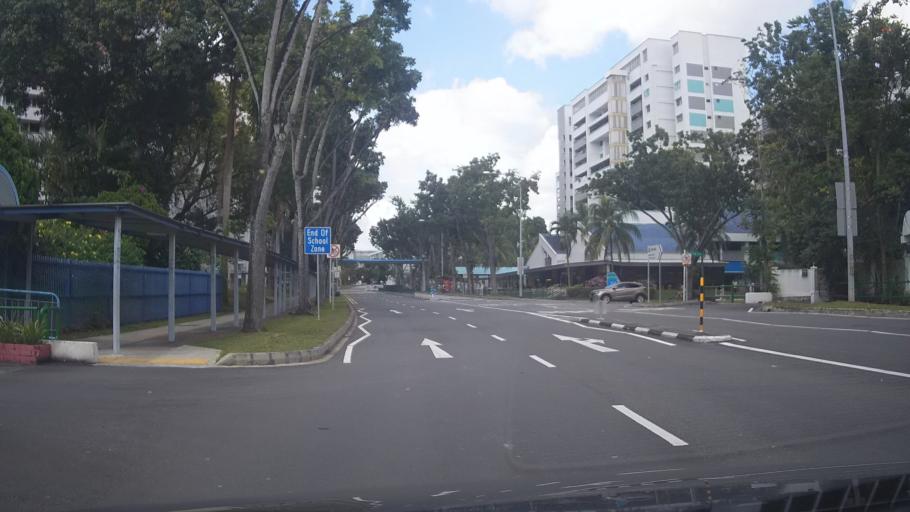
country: MY
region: Johor
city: Johor Bahru
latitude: 1.4456
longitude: 103.7745
